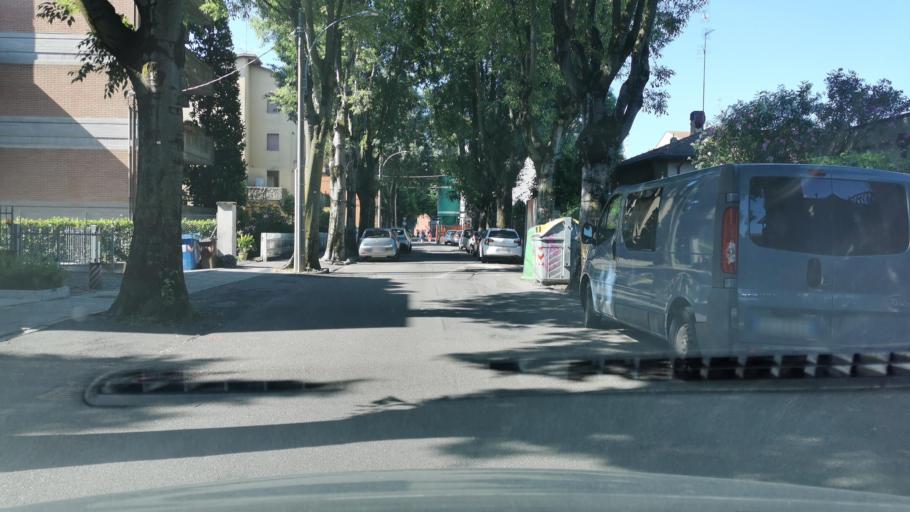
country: IT
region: Emilia-Romagna
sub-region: Provincia di Modena
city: Carpi Centro
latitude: 44.7875
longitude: 10.8877
